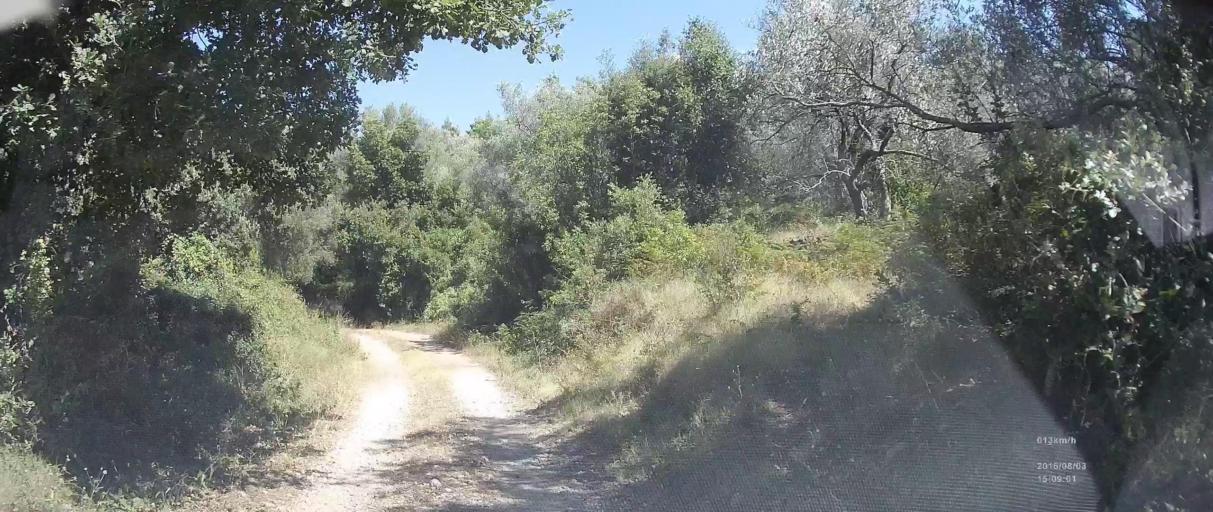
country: HR
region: Dubrovacko-Neretvanska
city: Blato
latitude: 42.7313
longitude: 17.5489
